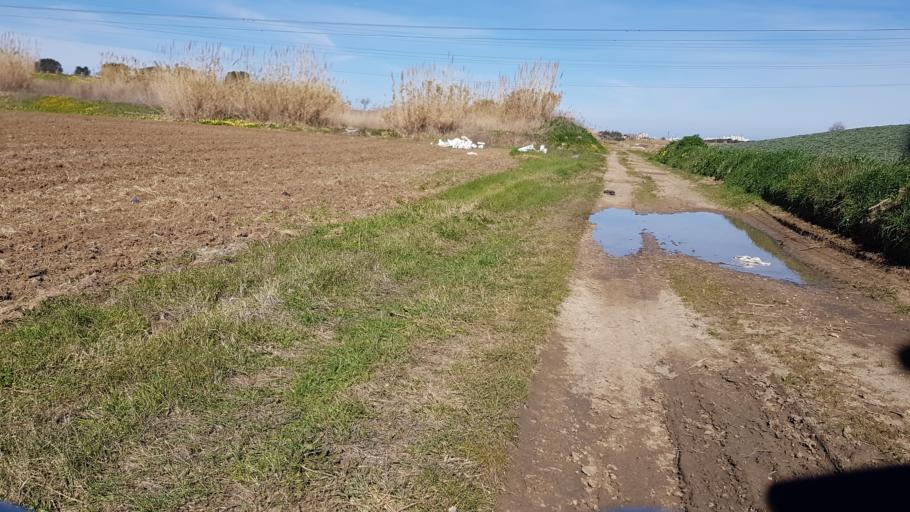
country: IT
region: Apulia
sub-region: Provincia di Brindisi
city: La Rosa
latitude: 40.5971
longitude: 17.9277
